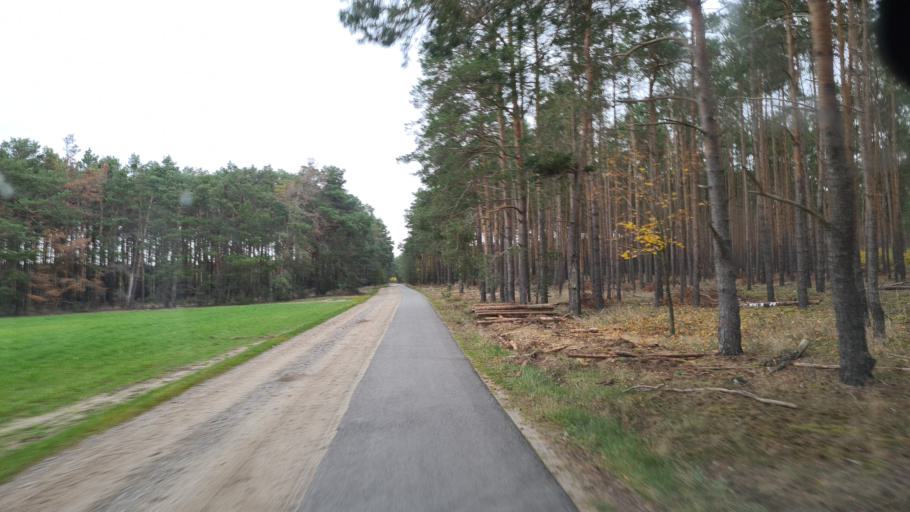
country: DE
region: Brandenburg
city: Finsterwalde
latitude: 51.6448
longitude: 13.7540
